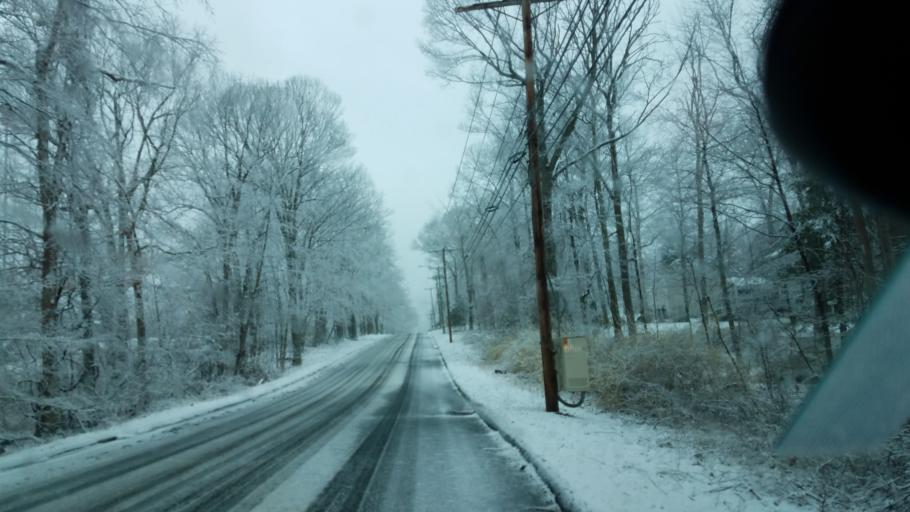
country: US
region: Connecticut
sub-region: New Haven County
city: Cheshire
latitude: 41.4880
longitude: -72.9264
